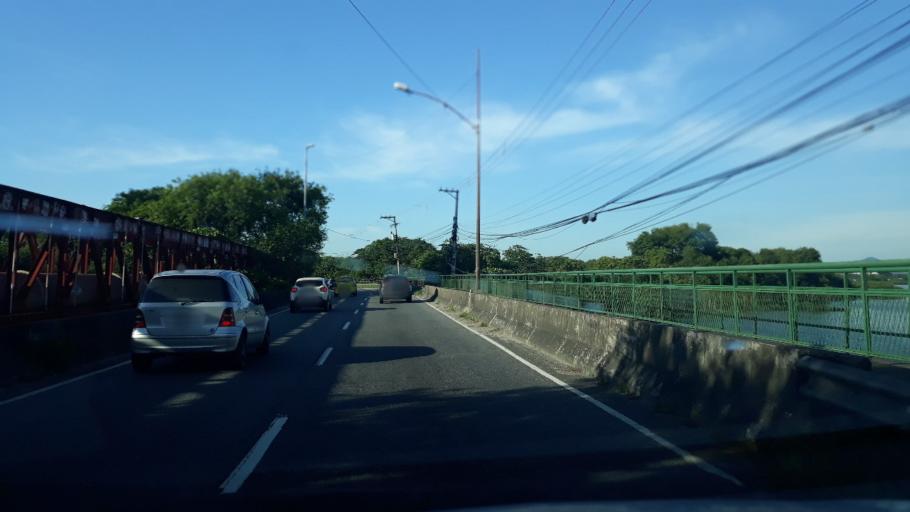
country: BR
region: Rio de Janeiro
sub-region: Sao Joao De Meriti
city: Sao Joao de Meriti
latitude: -22.9759
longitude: -43.3652
